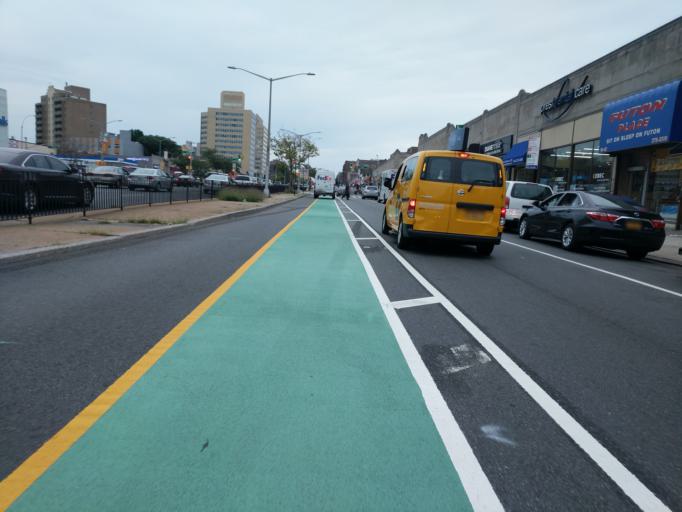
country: US
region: New York
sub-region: Queens County
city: Borough of Queens
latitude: 40.7303
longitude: -73.8634
